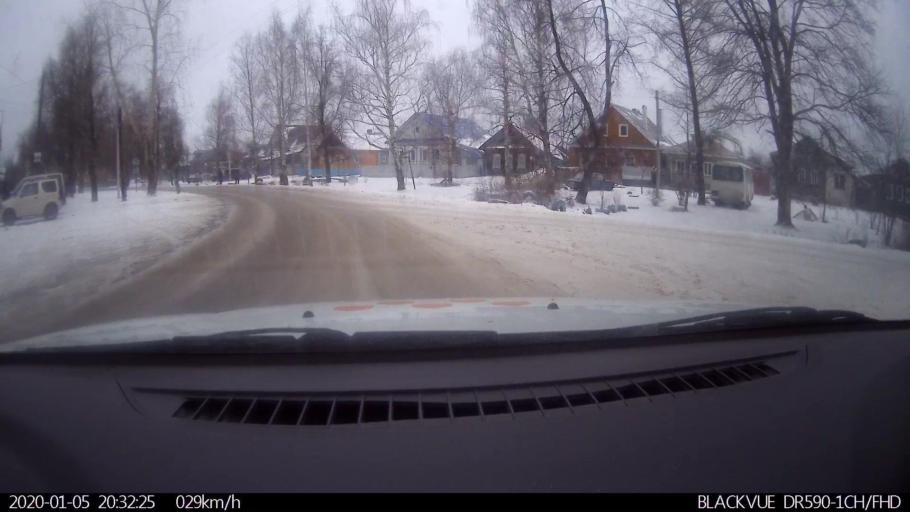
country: RU
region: Nizjnij Novgorod
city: Lukino
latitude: 56.4120
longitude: 43.7288
